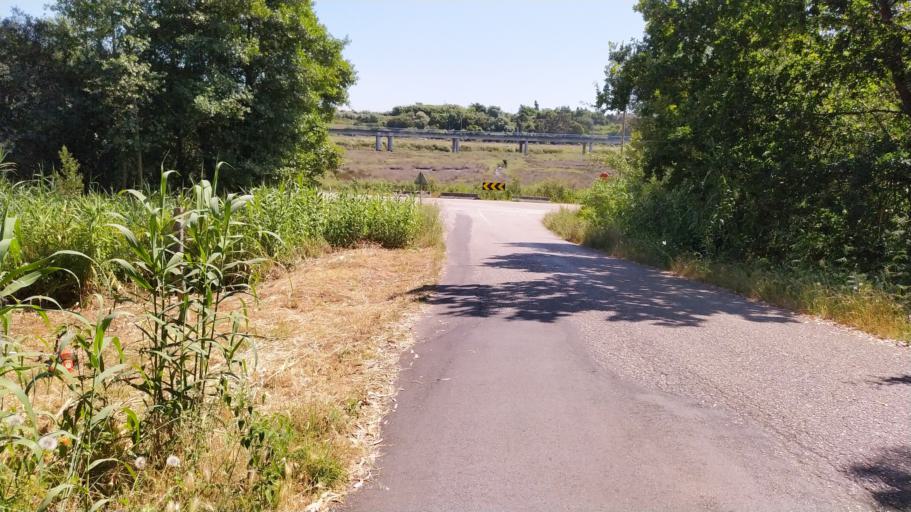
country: PT
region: Aveiro
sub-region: Aveiro
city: Aveiro
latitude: 40.6568
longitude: -8.6344
